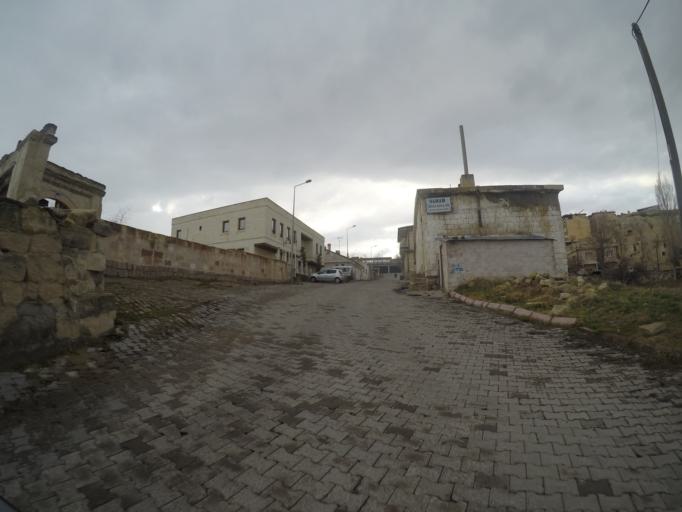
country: TR
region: Nevsehir
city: Goereme
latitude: 38.6221
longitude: 34.8672
